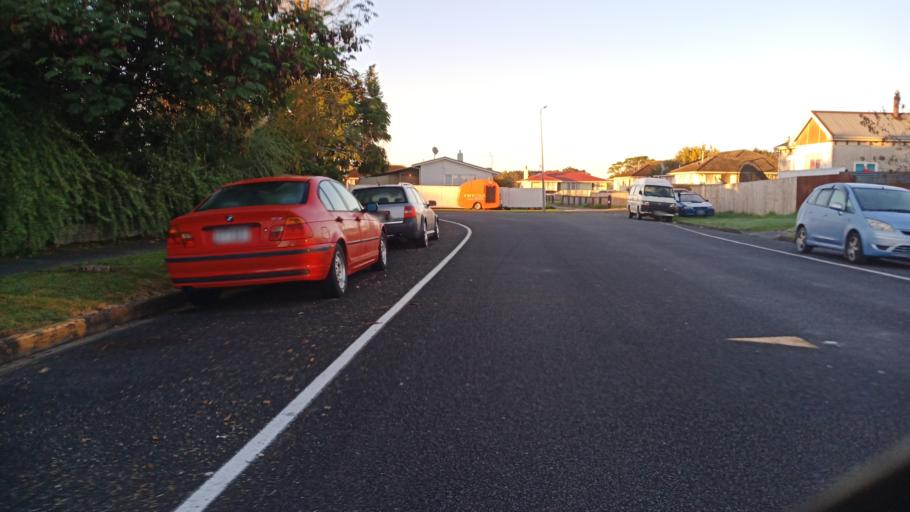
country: NZ
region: Gisborne
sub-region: Gisborne District
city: Gisborne
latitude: -38.6612
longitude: 177.9863
